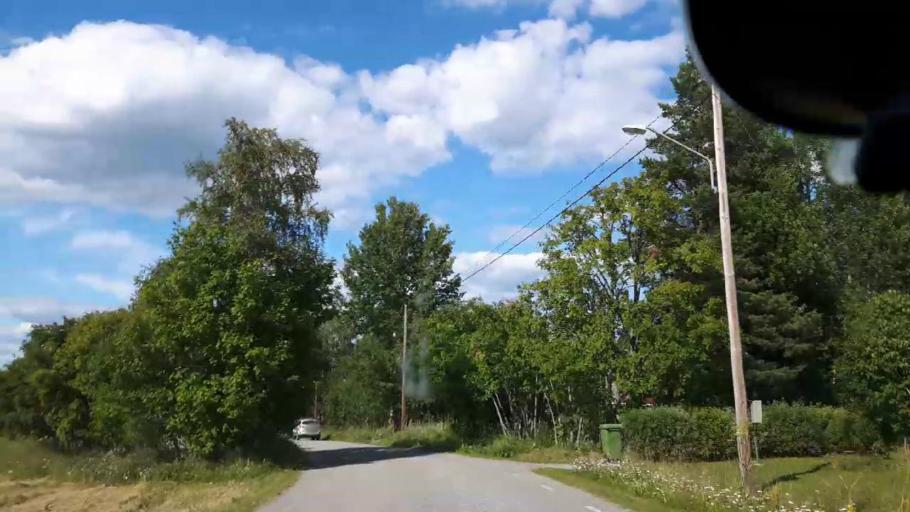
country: SE
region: Jaemtland
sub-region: Braecke Kommun
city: Braecke
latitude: 62.8786
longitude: 15.2756
